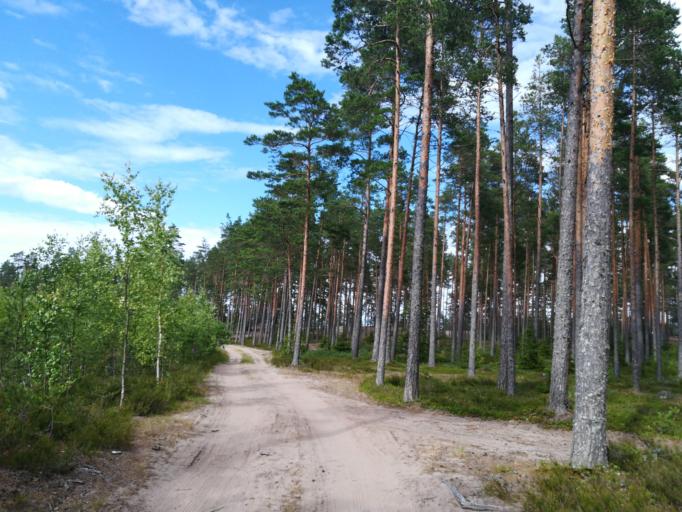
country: RU
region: Leningrad
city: Ust'-Luga
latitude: 59.6797
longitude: 28.2293
